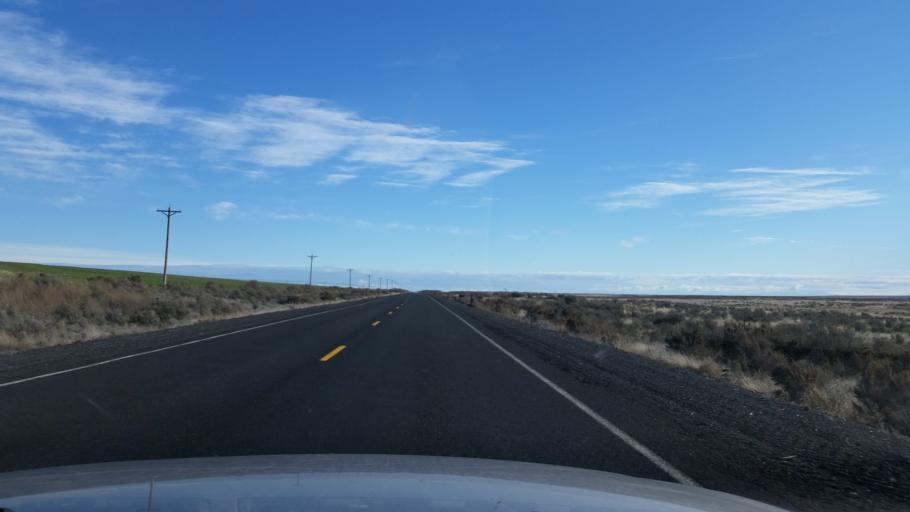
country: US
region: Washington
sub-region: Grant County
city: Warden
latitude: 47.3365
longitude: -118.8964
